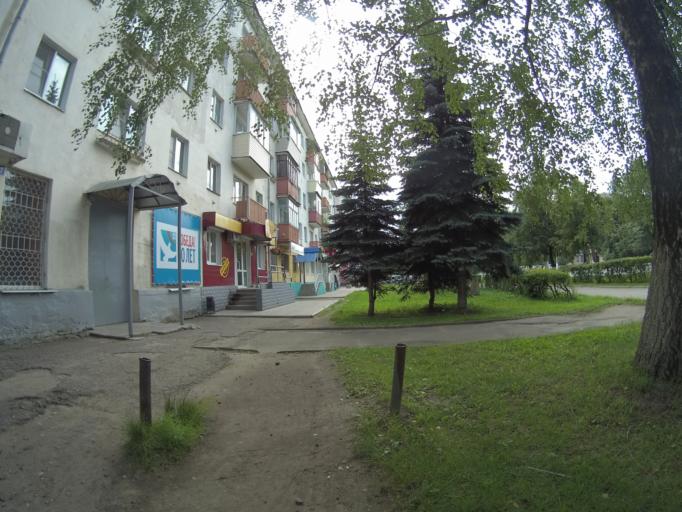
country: RU
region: Vladimir
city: Vladimir
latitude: 56.1214
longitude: 40.3809
